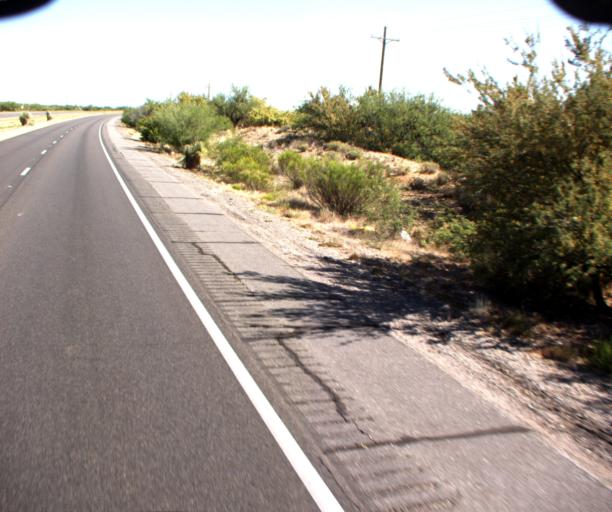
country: US
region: Arizona
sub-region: Pima County
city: Catalina
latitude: 32.5350
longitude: -110.9304
